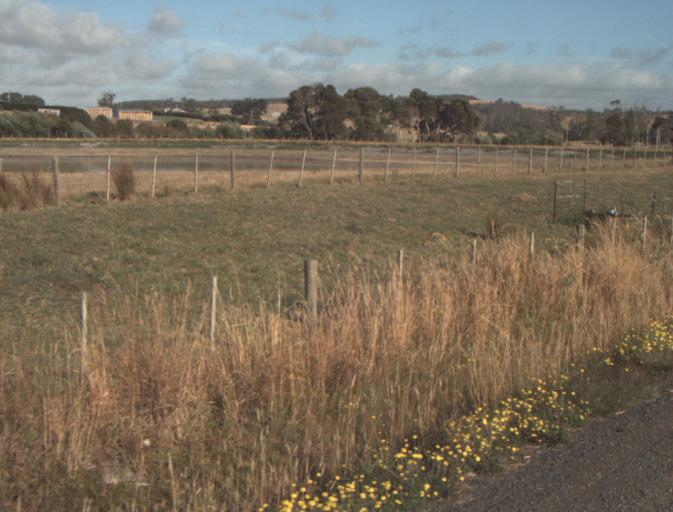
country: AU
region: Tasmania
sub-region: Launceston
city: Mayfield
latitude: -41.2412
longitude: 147.2162
